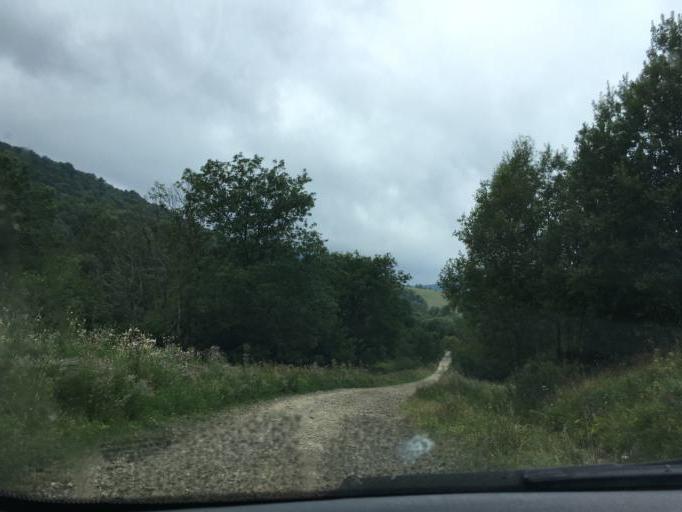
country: PL
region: Subcarpathian Voivodeship
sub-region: Powiat bieszczadzki
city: Lutowiska
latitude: 49.1654
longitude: 22.6206
